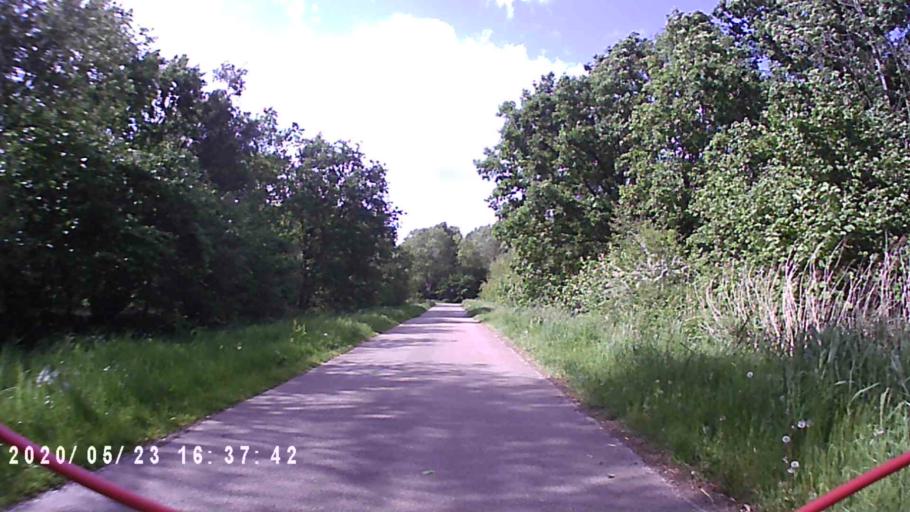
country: NL
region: Groningen
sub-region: Gemeente Slochteren
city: Slochteren
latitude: 53.2647
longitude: 6.8305
